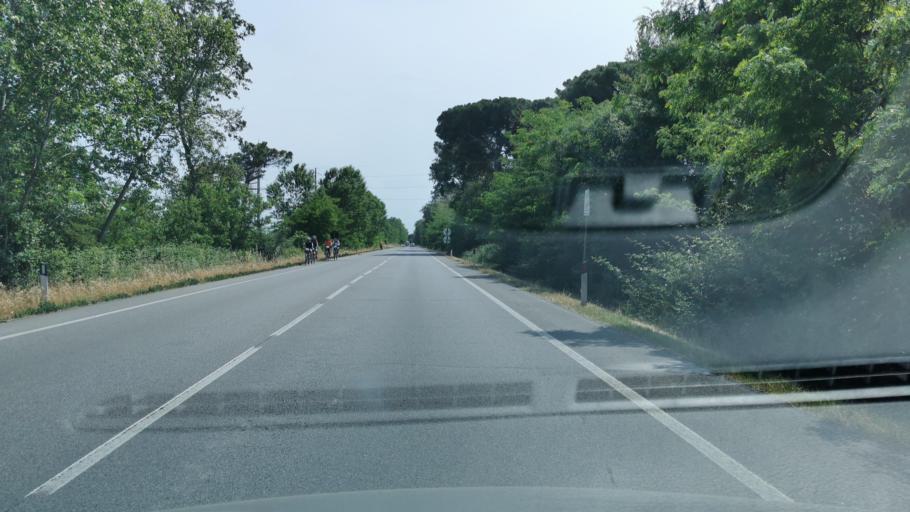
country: IT
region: Emilia-Romagna
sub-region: Provincia di Ferrara
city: Lido degli Estensi
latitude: 44.6176
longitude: 12.2448
